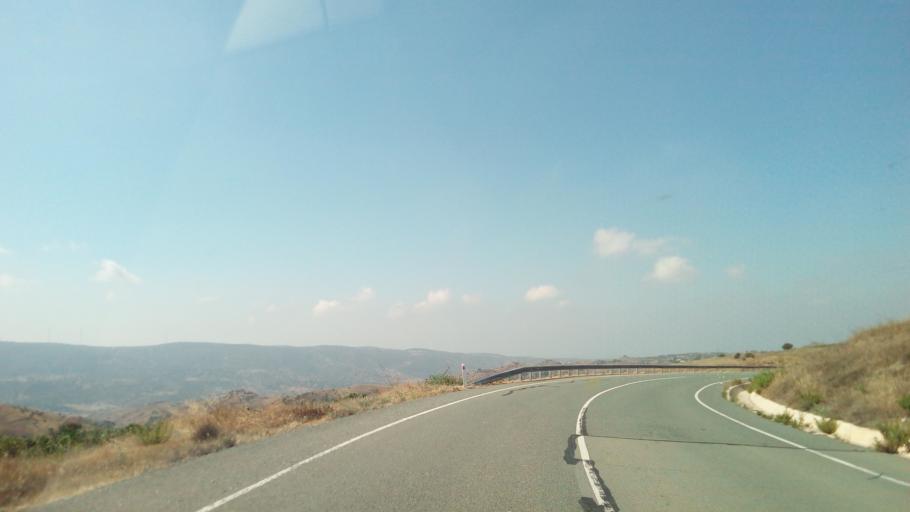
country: CY
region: Limassol
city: Pissouri
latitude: 34.7824
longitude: 32.6120
